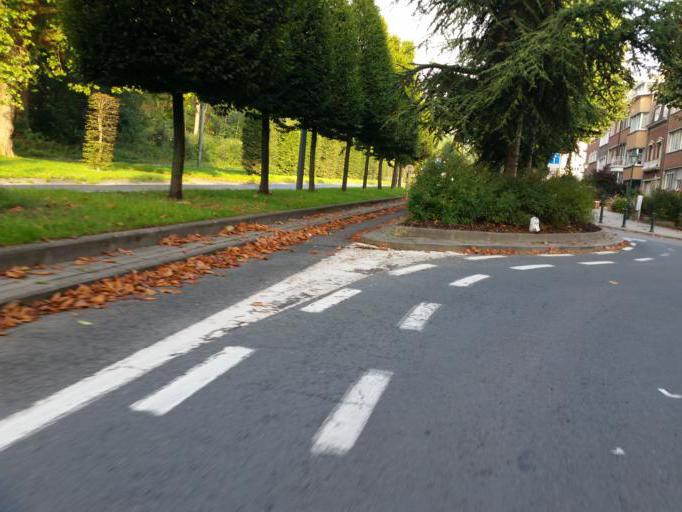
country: BE
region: Flanders
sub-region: Provincie Vlaams-Brabant
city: Grimbergen
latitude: 50.8923
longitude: 4.3665
